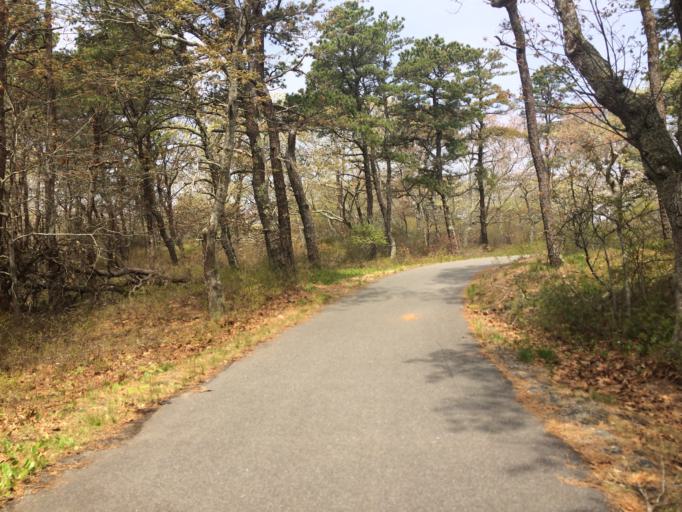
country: US
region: Massachusetts
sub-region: Barnstable County
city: Provincetown
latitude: 42.0672
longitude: -70.1918
